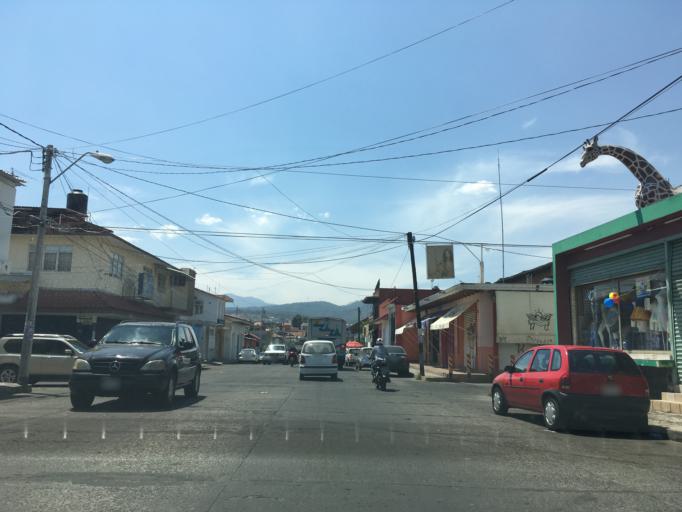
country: MX
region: Michoacan
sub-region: Uruapan
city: Uruapan
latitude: 19.4165
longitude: -102.0573
